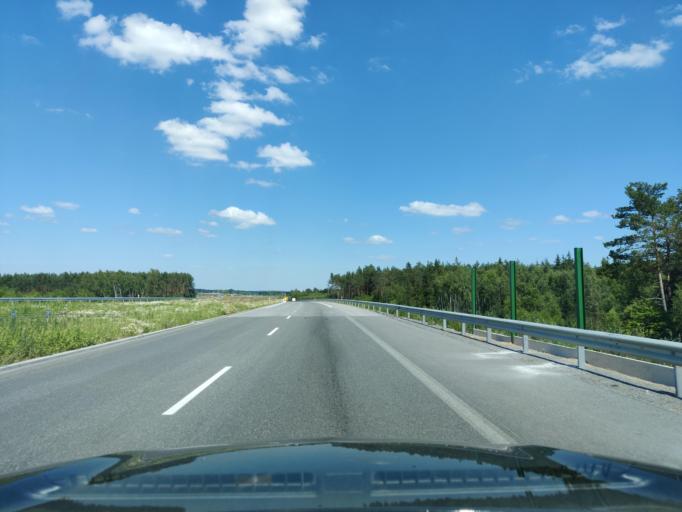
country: PL
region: Masovian Voivodeship
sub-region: Powiat mlawski
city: Wisniewo
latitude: 52.9800
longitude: 20.3373
